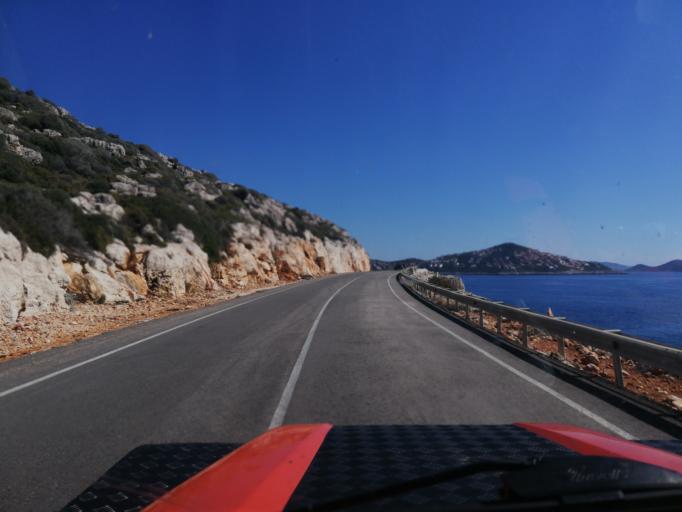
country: GR
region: South Aegean
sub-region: Nomos Dodekanisou
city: Megisti
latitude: 36.2039
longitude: 29.5723
